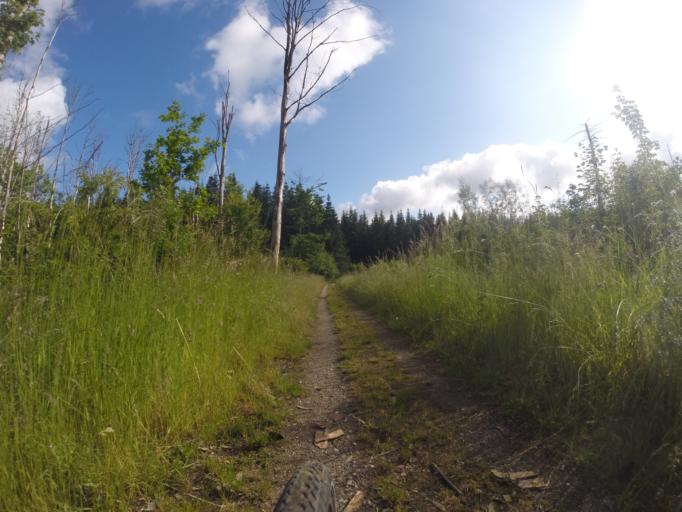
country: DK
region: Capital Region
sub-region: Ballerup Kommune
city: Ballerup
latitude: 55.6952
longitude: 12.3351
